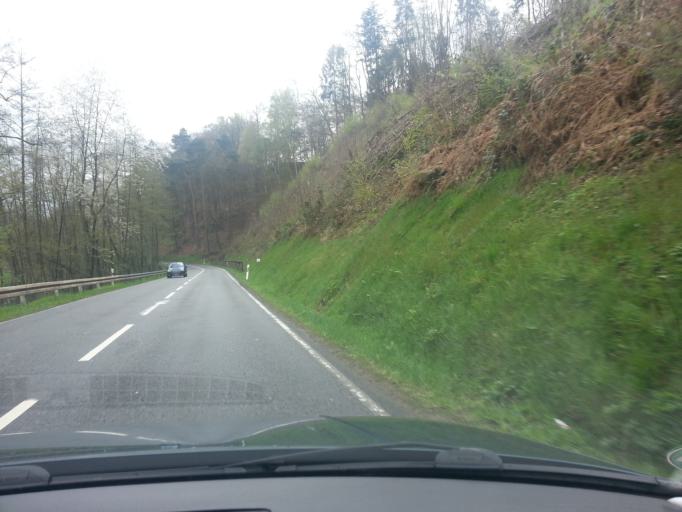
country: DE
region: Saarland
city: Homburg
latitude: 49.2920
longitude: 7.3026
